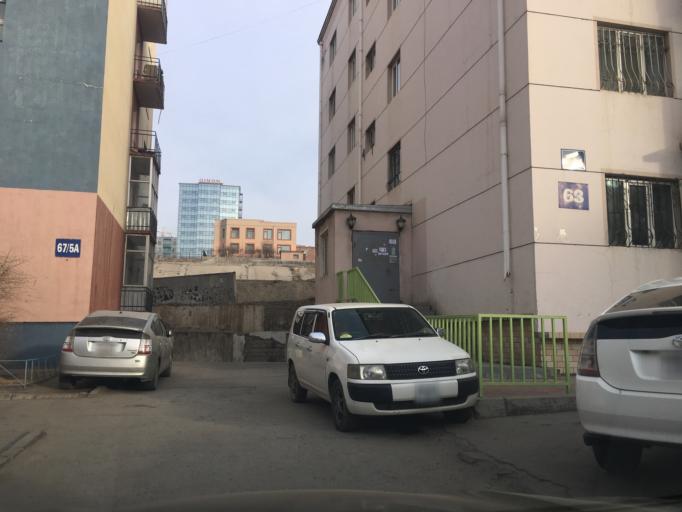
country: MN
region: Ulaanbaatar
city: Ulaanbaatar
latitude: 47.9165
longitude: 106.8801
